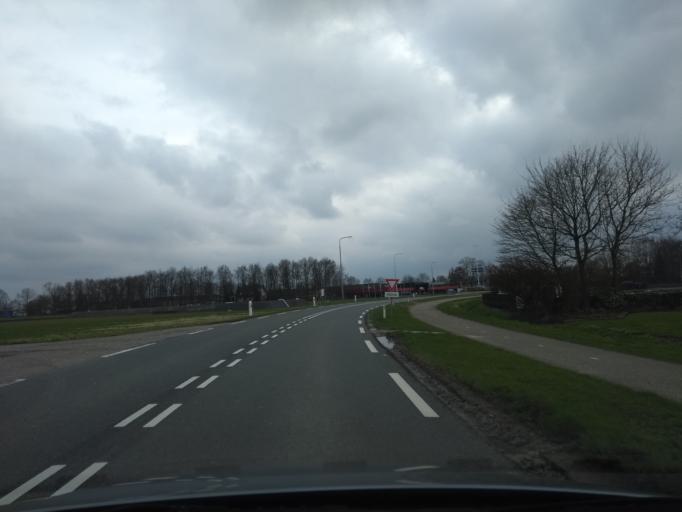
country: NL
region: Flevoland
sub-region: Gemeente Noordoostpolder
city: Ens
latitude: 52.7145
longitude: 5.8687
